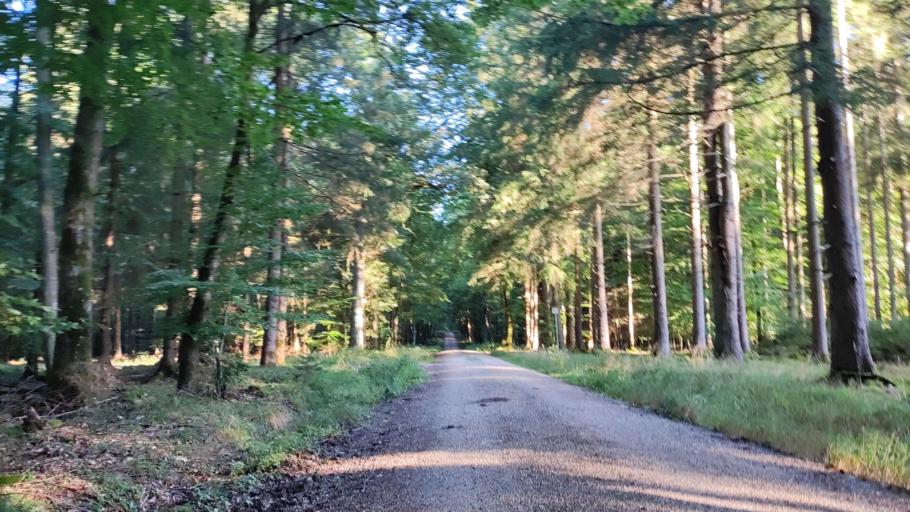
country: DE
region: Bavaria
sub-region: Swabia
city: Welden
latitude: 48.4237
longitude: 10.6417
